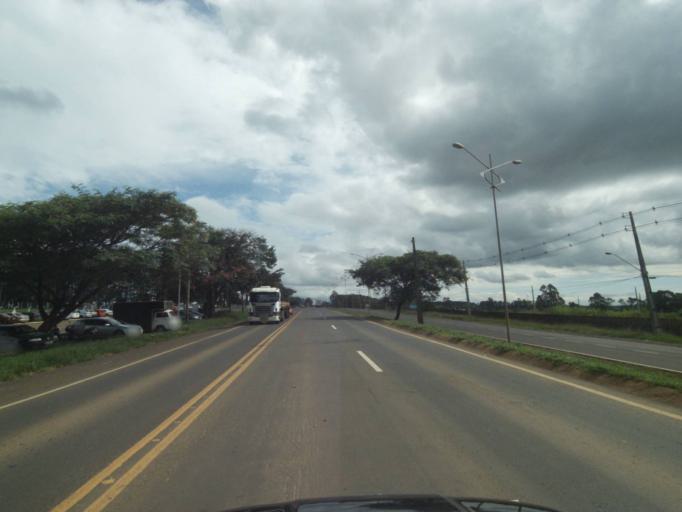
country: BR
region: Parana
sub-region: Telemaco Borba
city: Telemaco Borba
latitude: -24.3385
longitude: -50.6565
